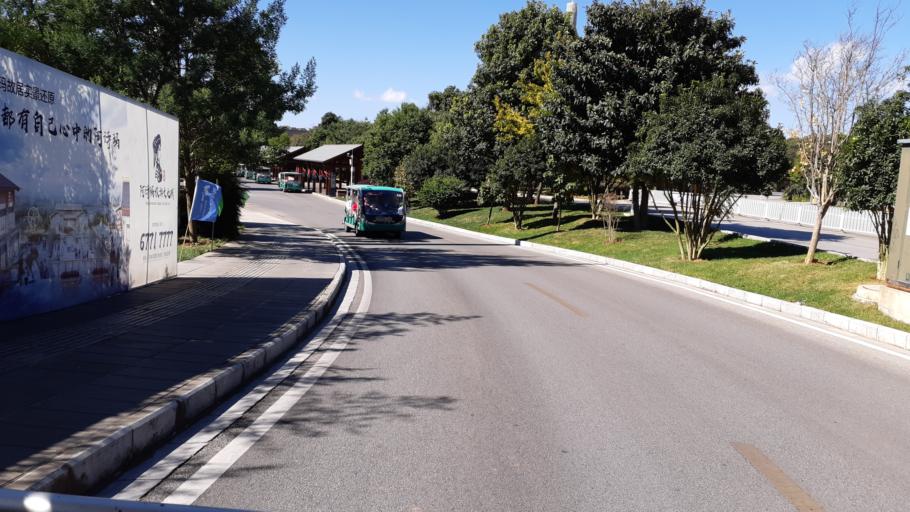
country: CN
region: Yunnan
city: Shilin
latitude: 24.8396
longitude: 103.3302
